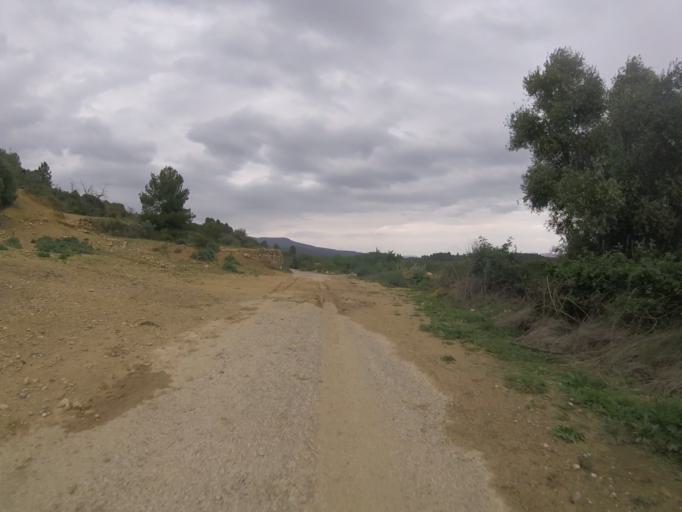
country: ES
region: Valencia
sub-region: Provincia de Castello
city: Sarratella
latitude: 40.2674
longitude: 0.0697
